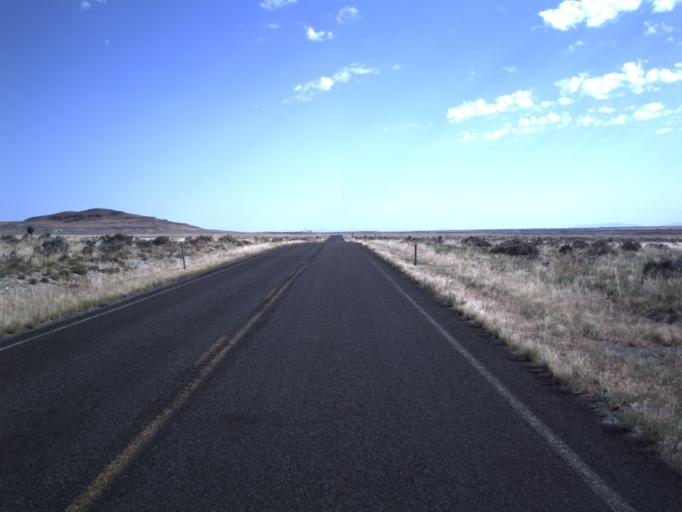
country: US
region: Utah
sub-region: Beaver County
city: Milford
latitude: 38.8424
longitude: -112.8450
